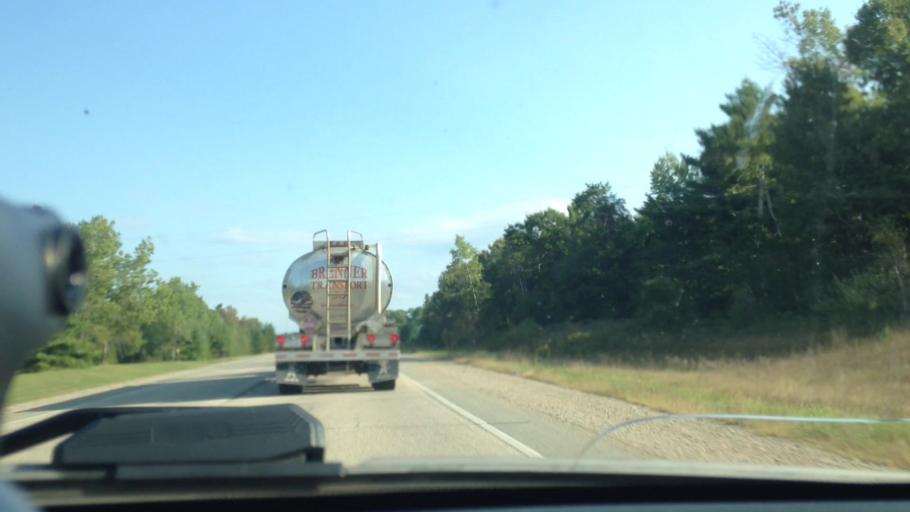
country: US
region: Wisconsin
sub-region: Marinette County
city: Niagara
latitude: 45.6543
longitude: -87.9628
